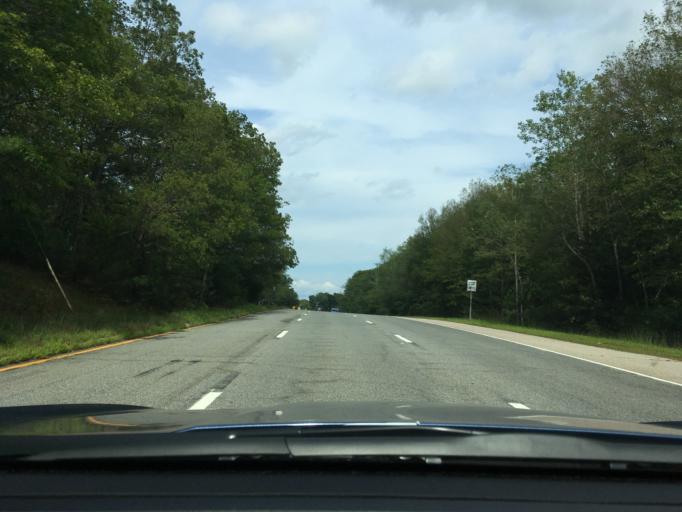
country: US
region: Rhode Island
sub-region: Kent County
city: East Greenwich
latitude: 41.6292
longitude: -71.4755
